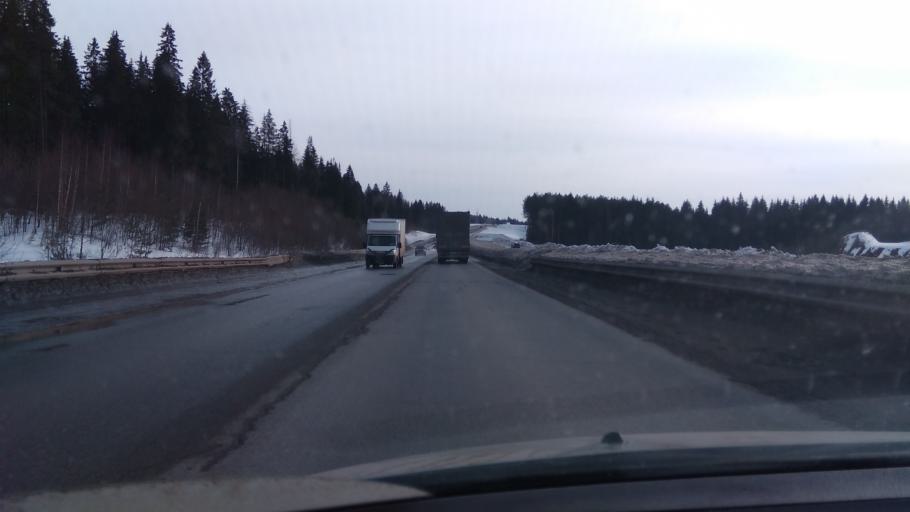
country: RU
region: Perm
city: Ferma
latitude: 57.9600
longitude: 56.3969
